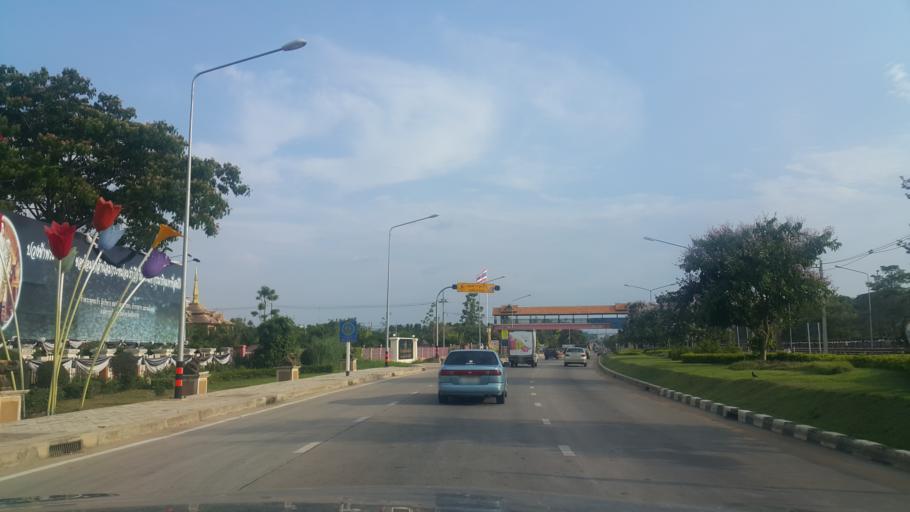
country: TH
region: Chiang Rai
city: Chiang Rai
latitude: 19.9299
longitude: 99.8639
